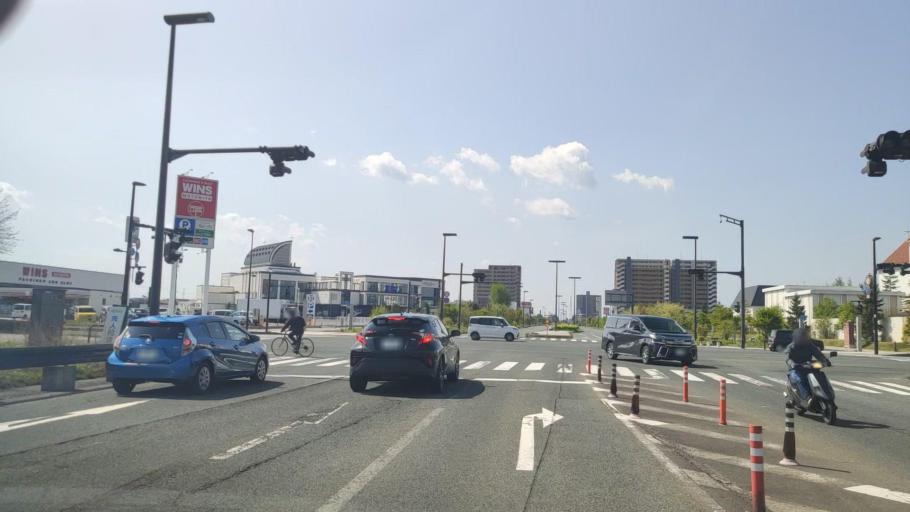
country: JP
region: Iwate
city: Morioka-shi
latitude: 39.6921
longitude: 141.1271
